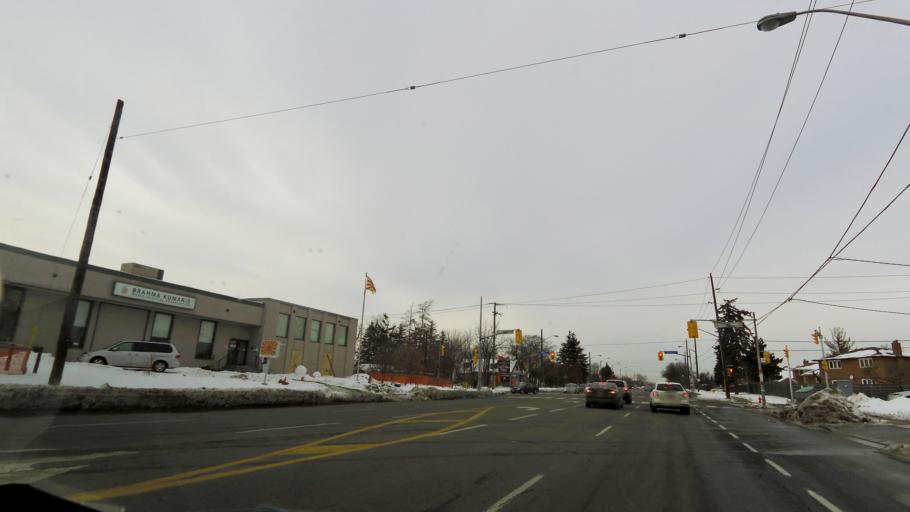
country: CA
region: Ontario
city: Concord
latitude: 43.7596
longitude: -79.5714
